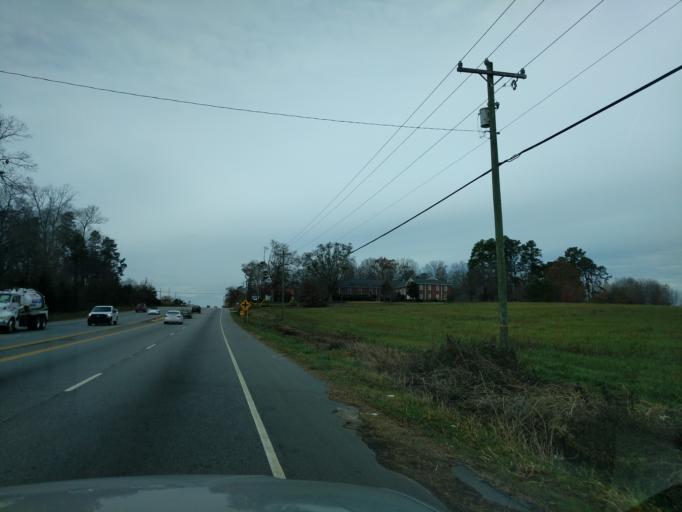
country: US
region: South Carolina
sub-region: Anderson County
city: Northlake
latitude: 34.5807
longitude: -82.7166
